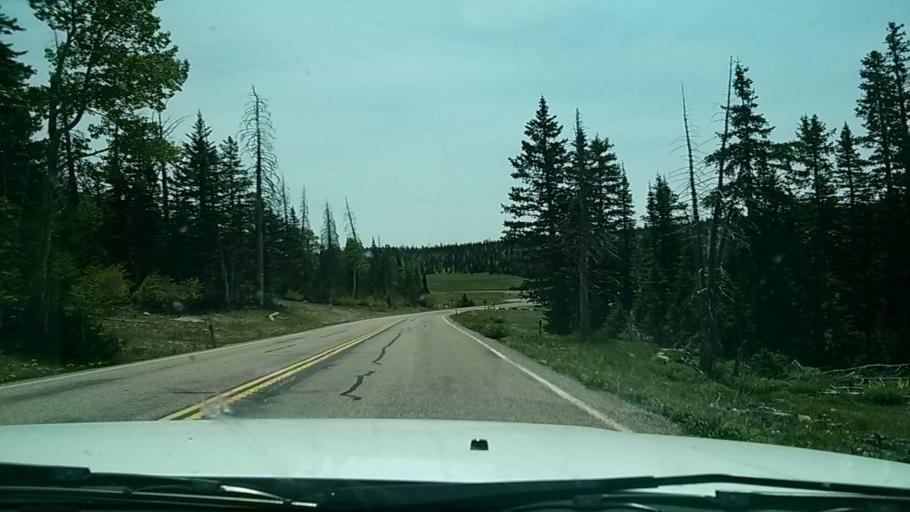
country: US
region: Utah
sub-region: Iron County
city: Cedar City
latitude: 37.5753
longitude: -112.8391
